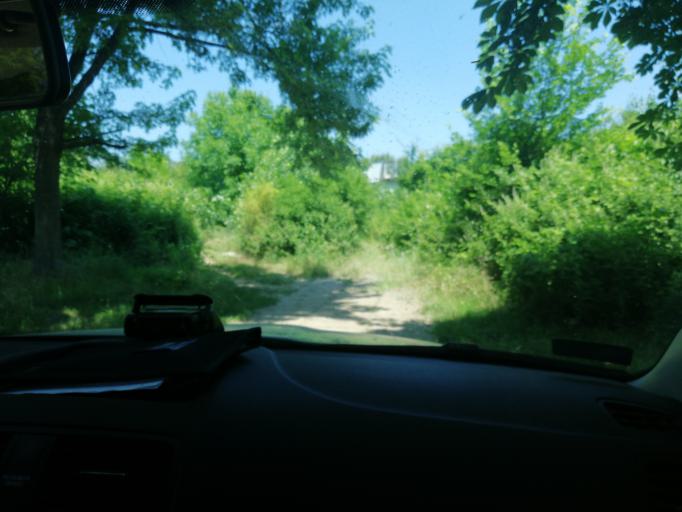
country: MK
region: Dojran
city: Star Dojran
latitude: 41.2517
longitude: 22.7389
